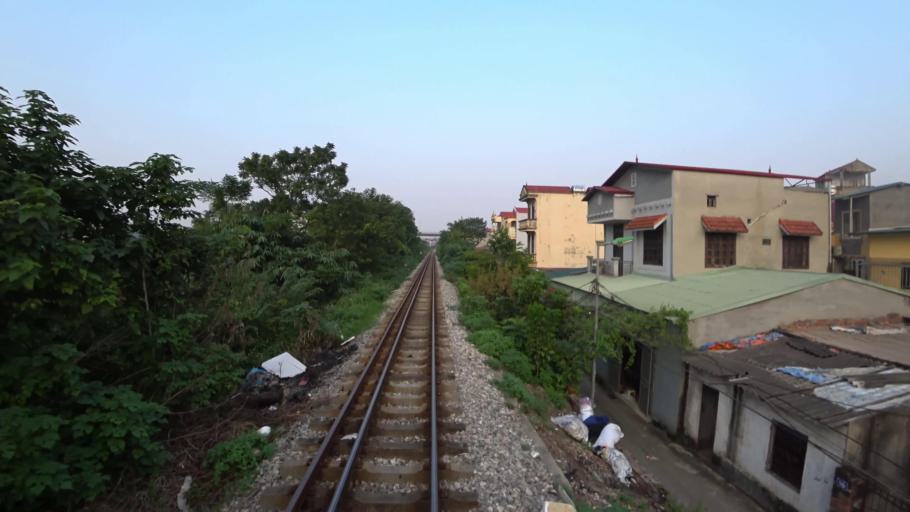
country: VN
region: Ha Noi
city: Trau Quy
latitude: 21.0709
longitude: 105.9021
